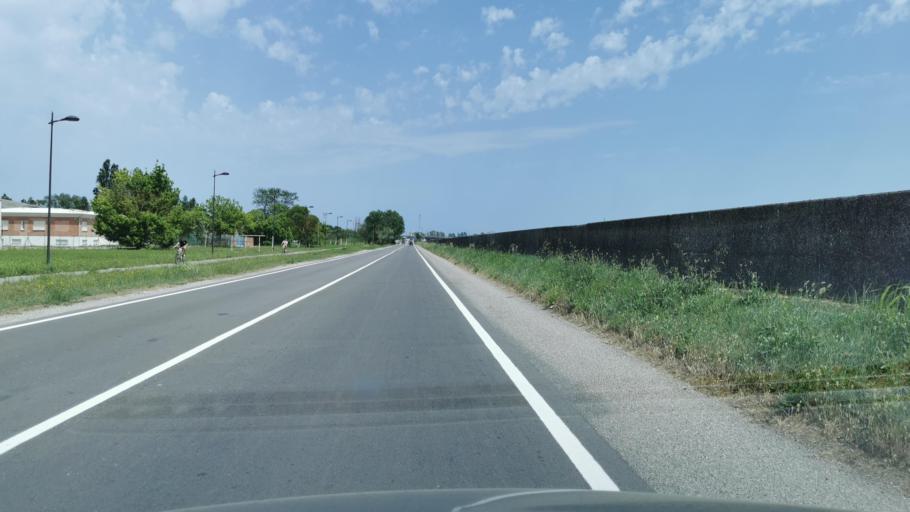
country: IT
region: Emilia-Romagna
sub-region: Provincia di Ferrara
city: Porto Garibaldi
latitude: 44.6767
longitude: 12.2165
